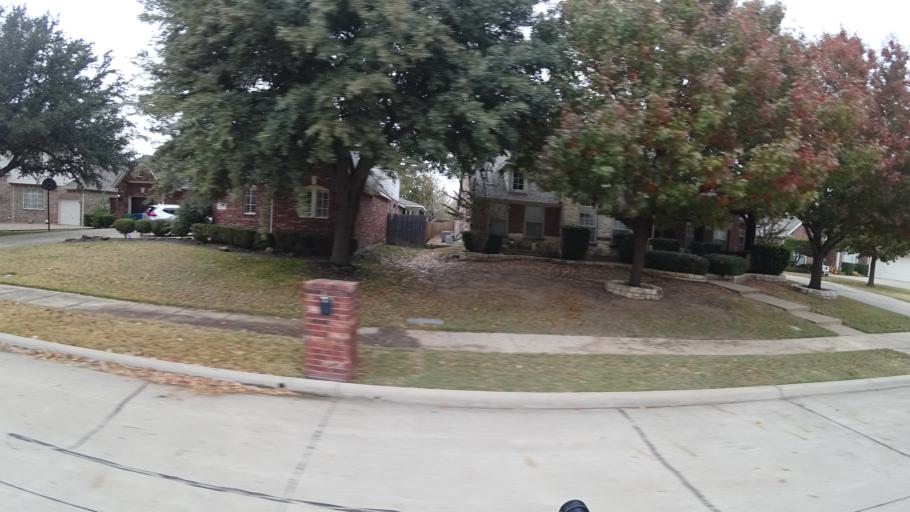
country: US
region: Texas
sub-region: Denton County
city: Lewisville
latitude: 33.0333
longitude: -96.9375
